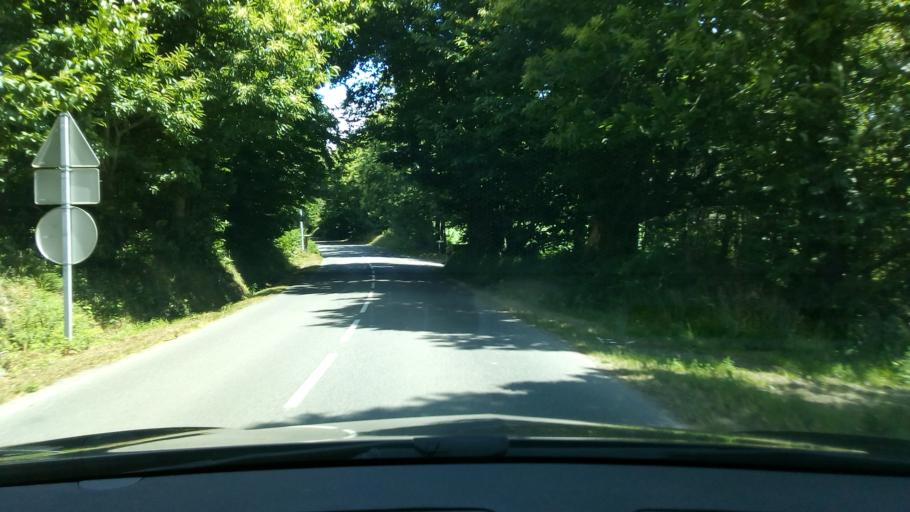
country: FR
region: Brittany
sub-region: Departement du Finistere
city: Melgven
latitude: 47.8843
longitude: -3.8258
